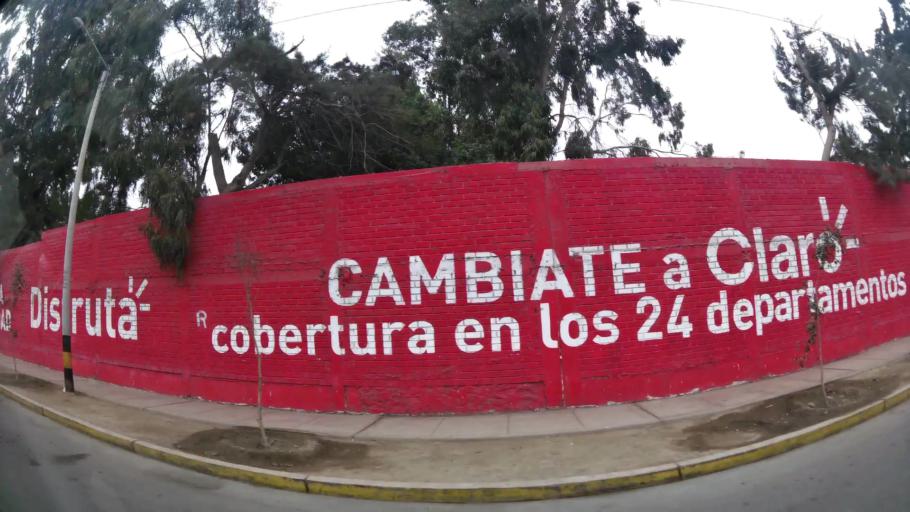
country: PE
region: Ica
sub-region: Provincia de Pisco
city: Pisco
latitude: -13.7120
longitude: -76.2078
